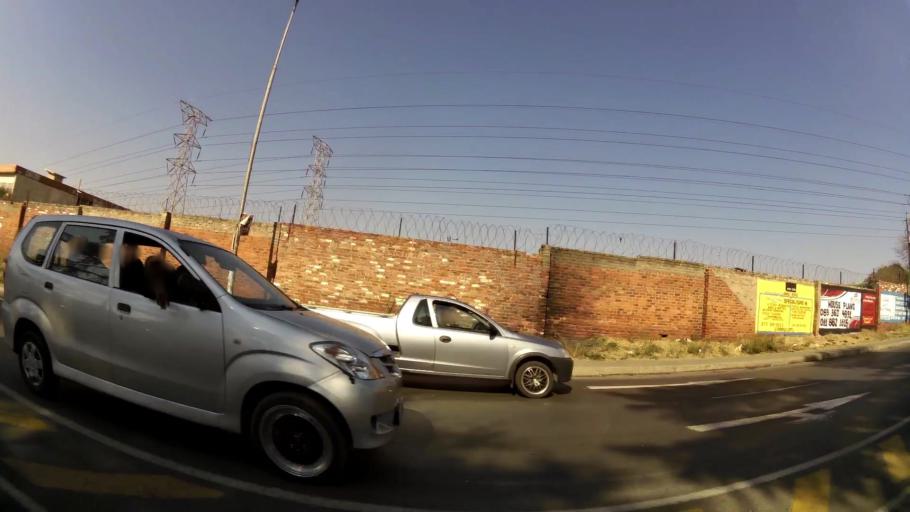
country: ZA
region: Gauteng
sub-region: City of Johannesburg Metropolitan Municipality
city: Modderfontein
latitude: -26.1162
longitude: 28.0900
